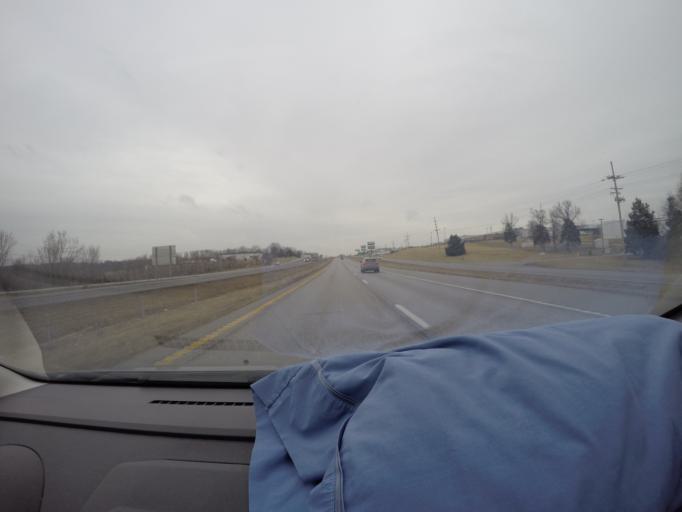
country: US
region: Missouri
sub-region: Warren County
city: Warrenton
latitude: 38.8182
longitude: -91.1264
